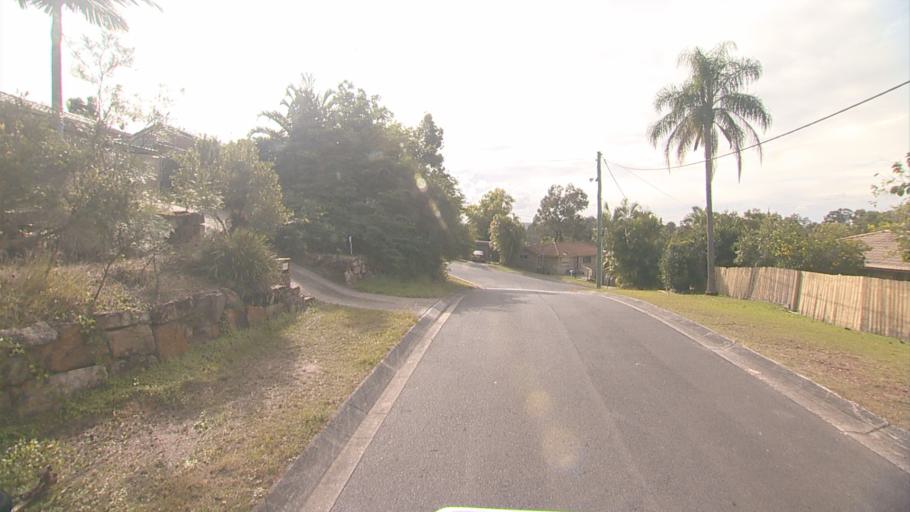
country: AU
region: Queensland
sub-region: Logan
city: Windaroo
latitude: -27.7237
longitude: 153.1819
